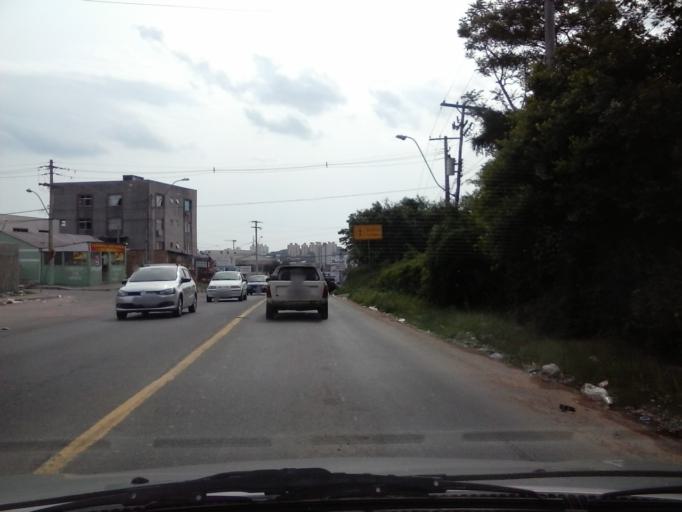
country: BR
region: Rio Grande do Sul
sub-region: Cachoeirinha
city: Cachoeirinha
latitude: -30.0383
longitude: -51.1203
